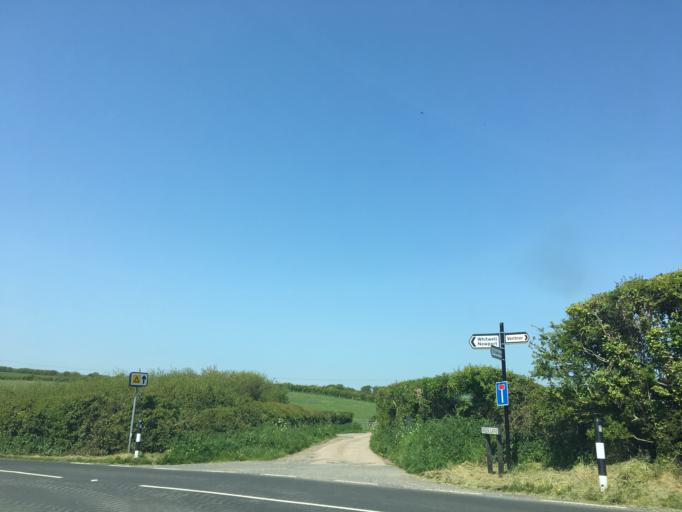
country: GB
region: England
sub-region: Isle of Wight
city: Niton
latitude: 50.5918
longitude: -1.2465
